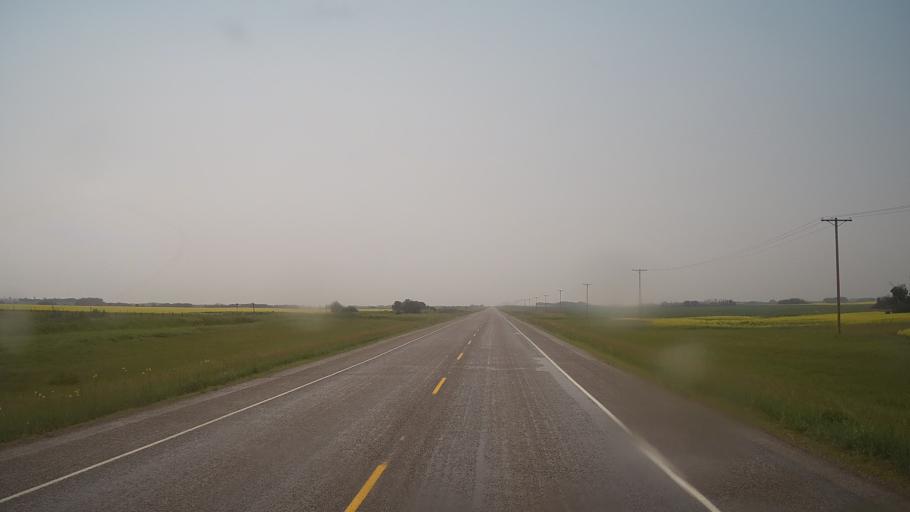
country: CA
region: Saskatchewan
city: Biggar
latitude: 52.1520
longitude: -108.2379
